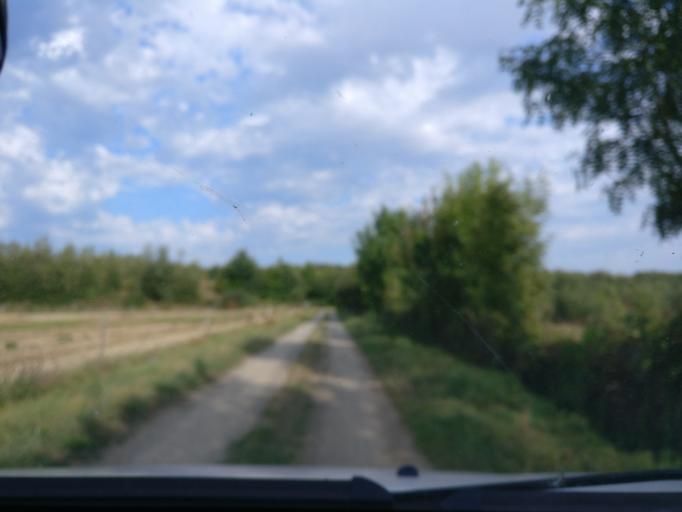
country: FR
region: Brittany
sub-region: Departement d'Ille-et-Vilaine
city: Fouillard
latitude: 48.1356
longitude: -1.5781
